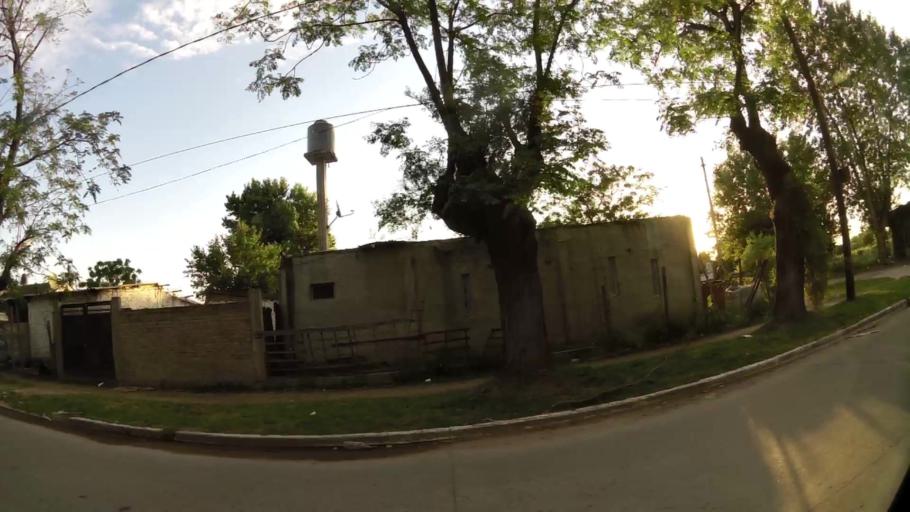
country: AR
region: Buenos Aires
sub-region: Partido de Merlo
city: Merlo
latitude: -34.6704
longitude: -58.7724
